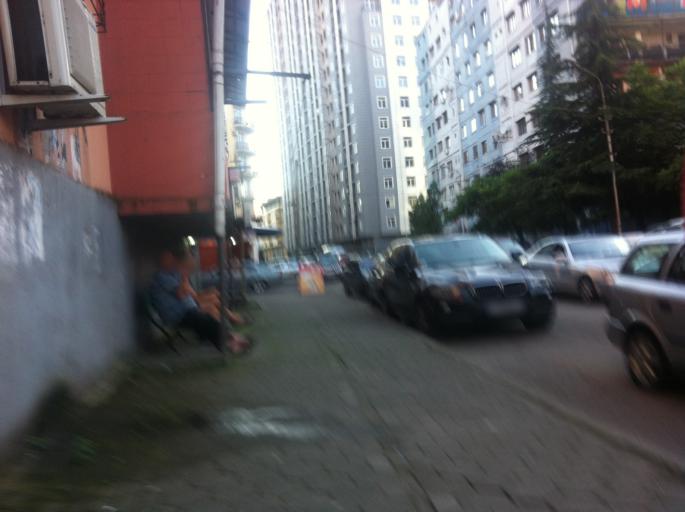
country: GE
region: Ajaria
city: Batumi
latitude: 41.6432
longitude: 41.6245
